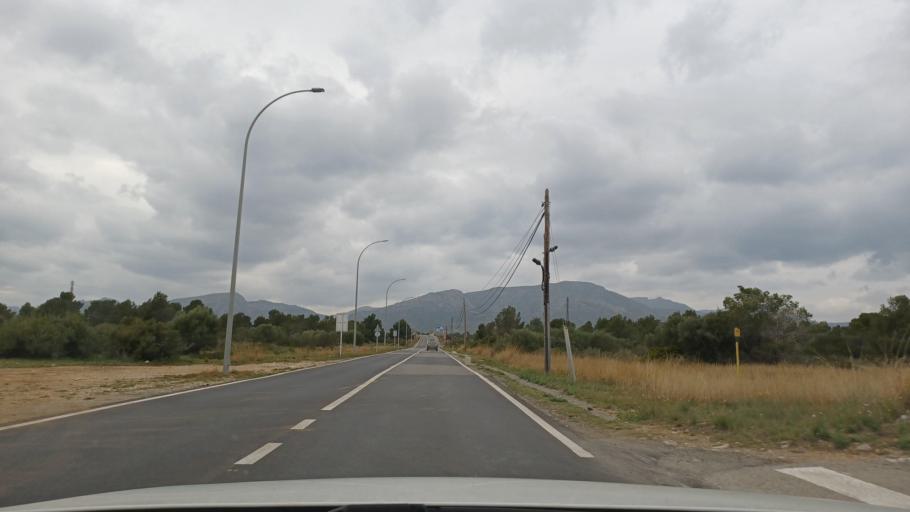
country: ES
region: Catalonia
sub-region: Provincia de Tarragona
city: Colldejou
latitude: 41.0214
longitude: 0.9353
